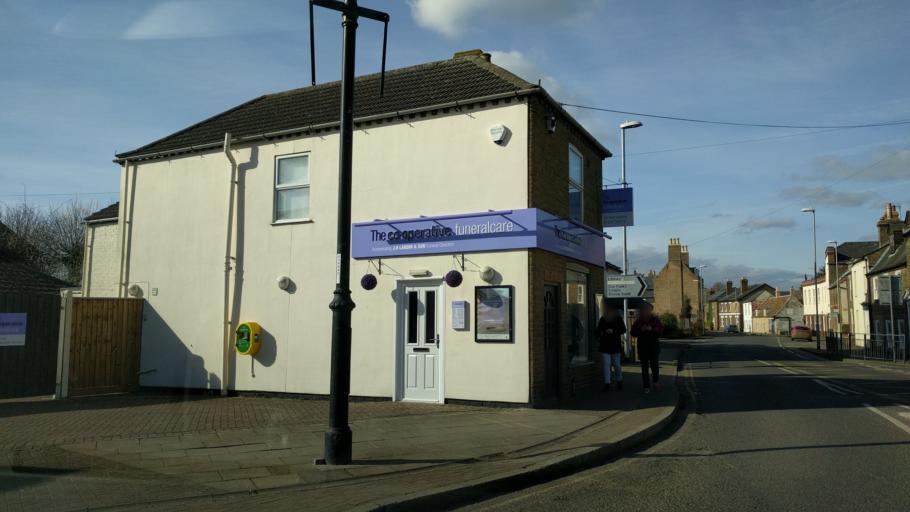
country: GB
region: England
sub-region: Cambridgeshire
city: Chatteris
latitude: 52.4573
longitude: 0.0476
